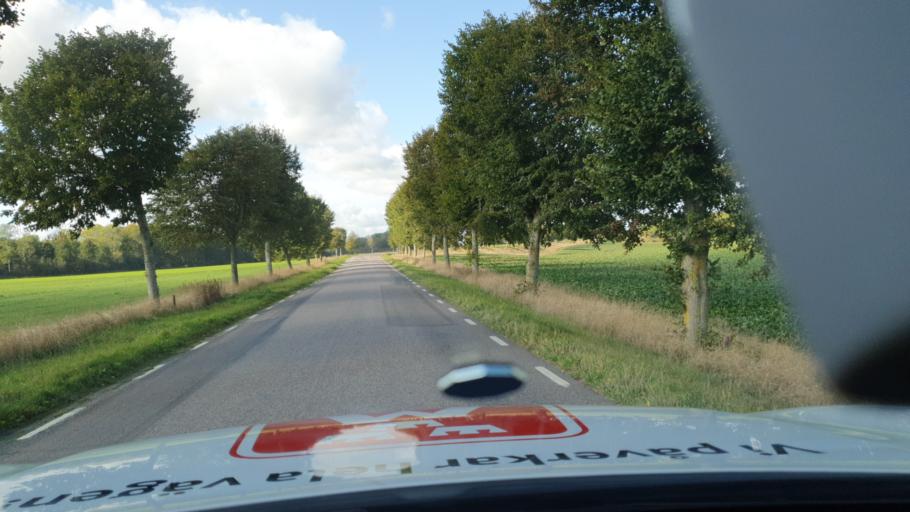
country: SE
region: Skane
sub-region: Ystads Kommun
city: Kopingebro
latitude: 55.4744
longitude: 13.9942
